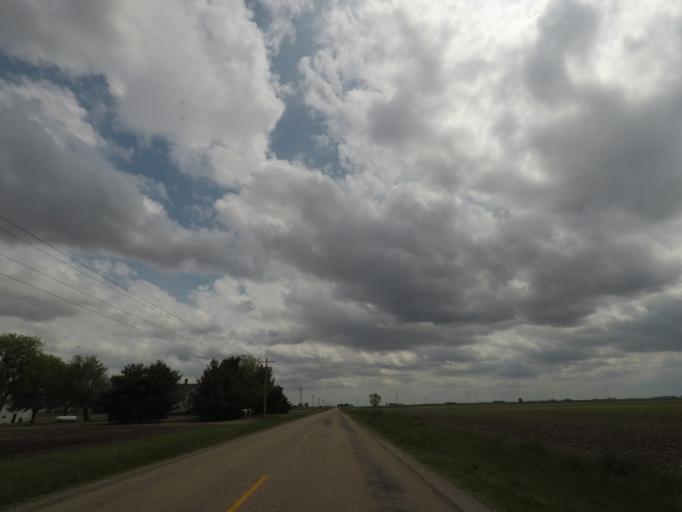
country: US
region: Illinois
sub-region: Macon County
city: Maroa
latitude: 40.0757
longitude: -89.0860
